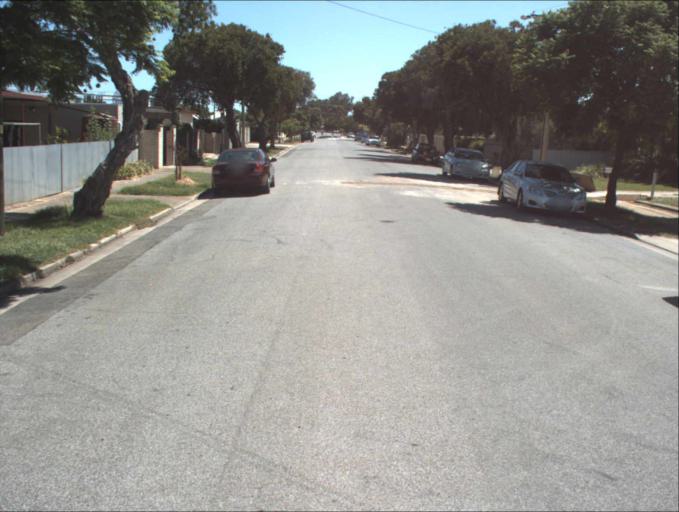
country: AU
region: South Australia
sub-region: Port Adelaide Enfield
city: Cheltenham
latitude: -34.8629
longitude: 138.5093
